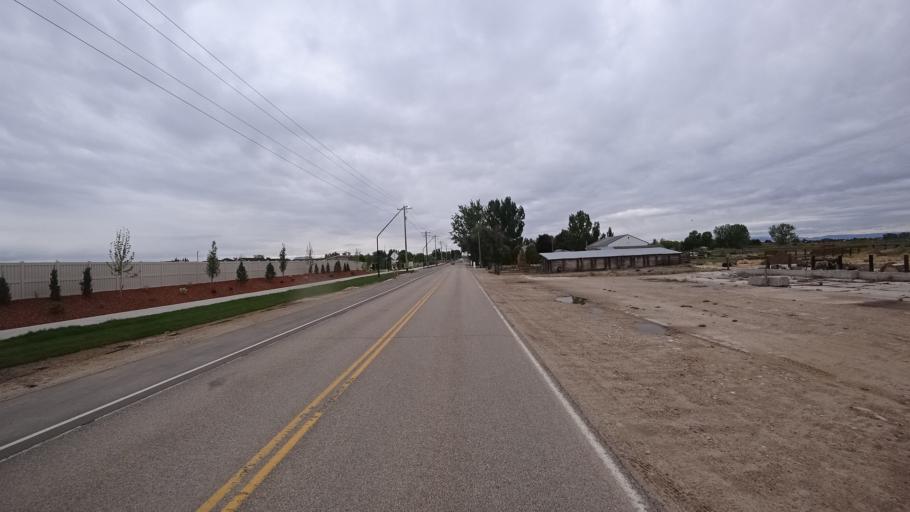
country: US
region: Idaho
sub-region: Ada County
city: Star
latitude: 43.6481
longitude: -116.4736
